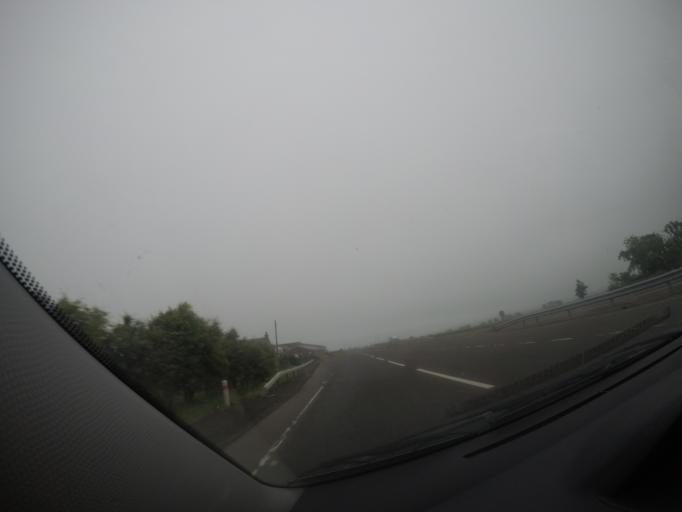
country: GB
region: Scotland
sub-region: Angus
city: Forfar
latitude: 56.5686
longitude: -2.9185
